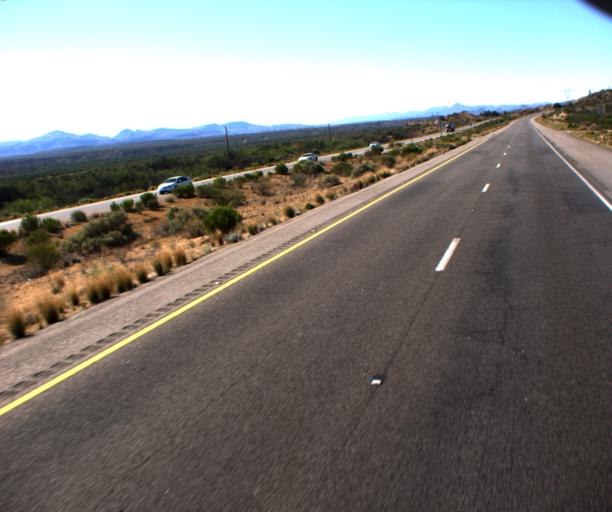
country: US
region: Arizona
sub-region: Yavapai County
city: Bagdad
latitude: 34.7621
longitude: -113.6182
